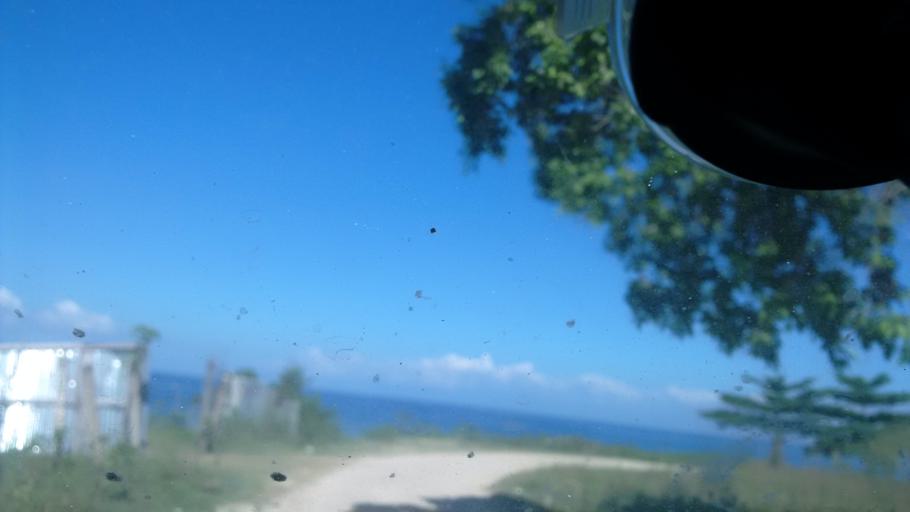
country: HT
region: Ouest
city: Grangwav
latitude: 18.4300
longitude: -72.7903
